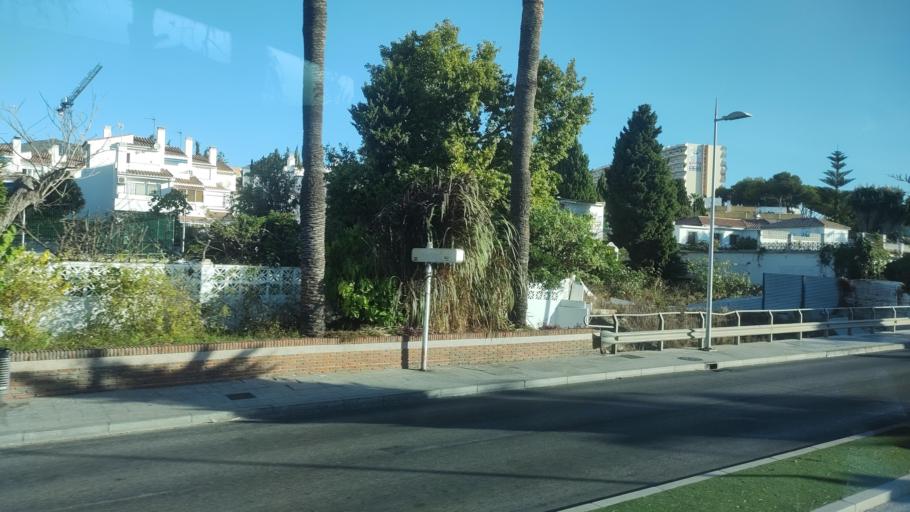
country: ES
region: Andalusia
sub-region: Provincia de Malaga
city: Torremolinos
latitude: 36.6013
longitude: -4.5151
